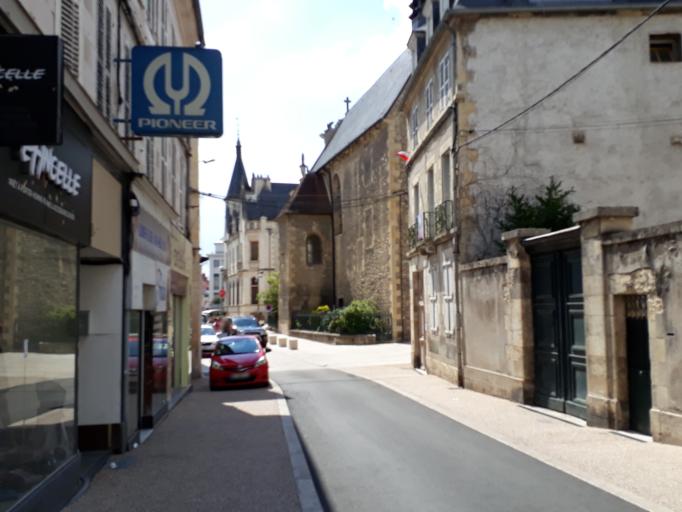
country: FR
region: Bourgogne
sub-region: Departement de la Nievre
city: Nevers
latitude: 46.9892
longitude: 3.1591
